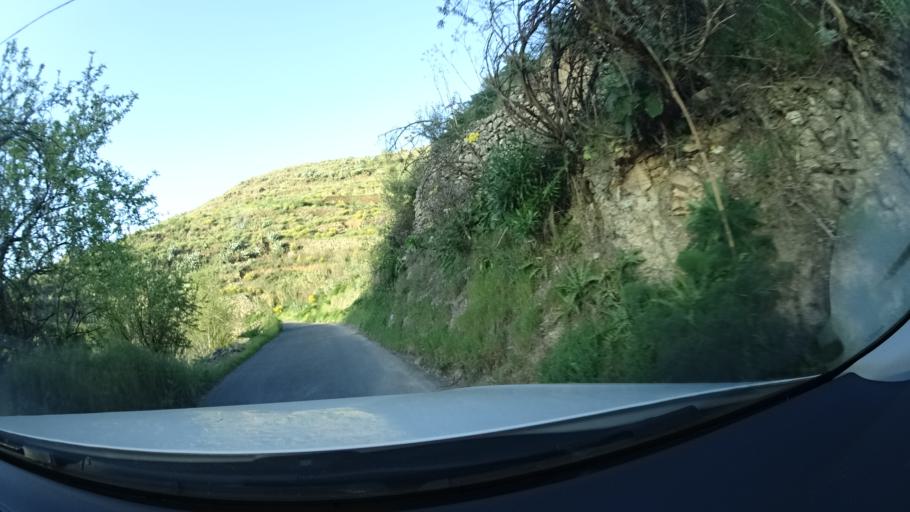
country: ES
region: Canary Islands
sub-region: Provincia de Las Palmas
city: Artenara
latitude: 28.0356
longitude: -15.6456
